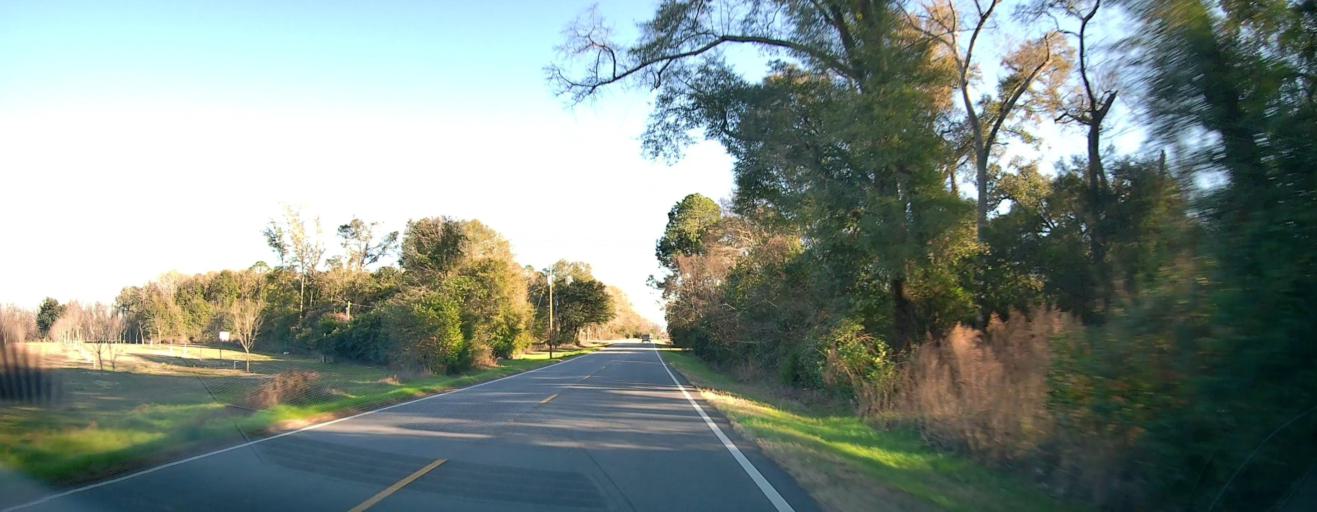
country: US
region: Georgia
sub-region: Dougherty County
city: Albany
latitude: 31.6398
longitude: -84.1671
